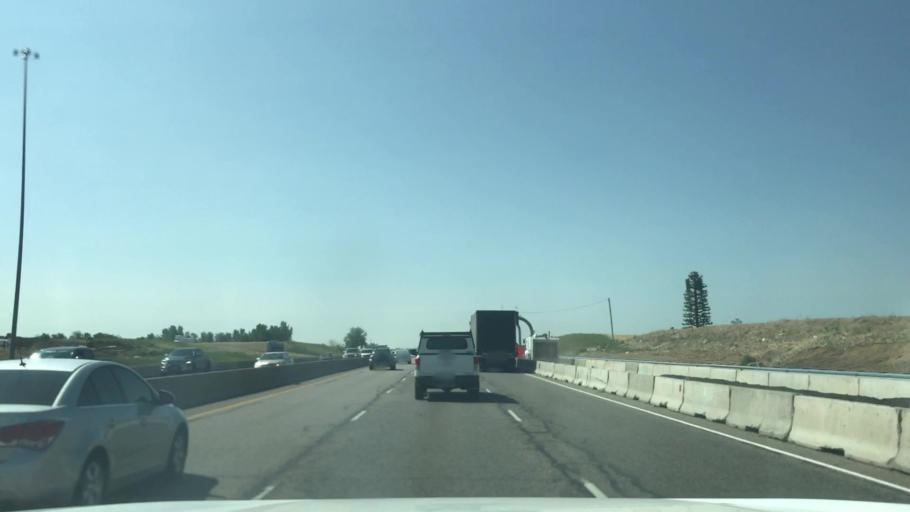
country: US
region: Colorado
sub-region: Adams County
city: Northglenn
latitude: 39.9734
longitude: -104.9882
